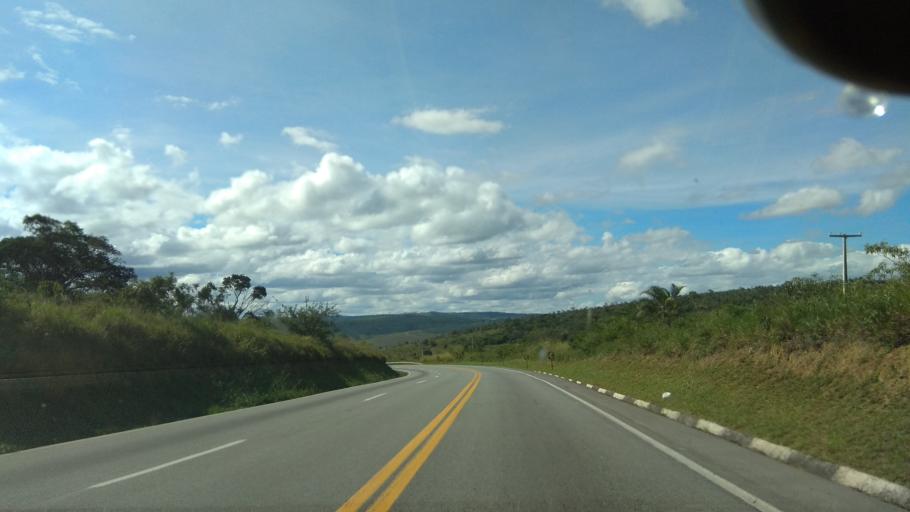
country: BR
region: Bahia
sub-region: Santa Ines
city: Santa Ines
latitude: -13.1907
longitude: -40.0077
